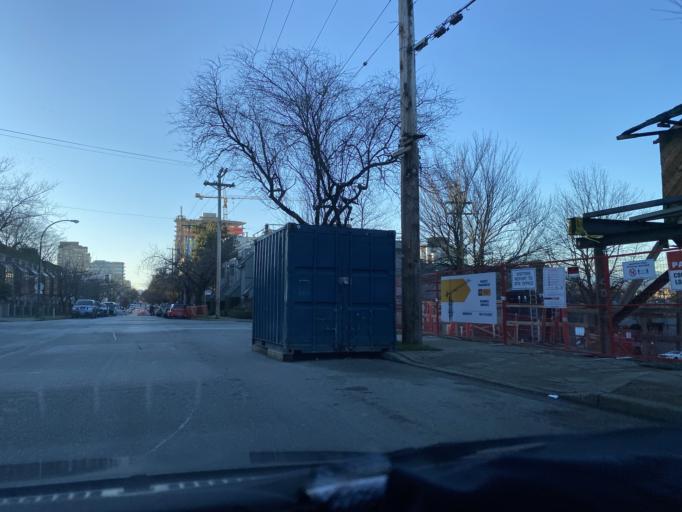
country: CA
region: British Columbia
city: West End
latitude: 49.2645
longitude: -123.1355
